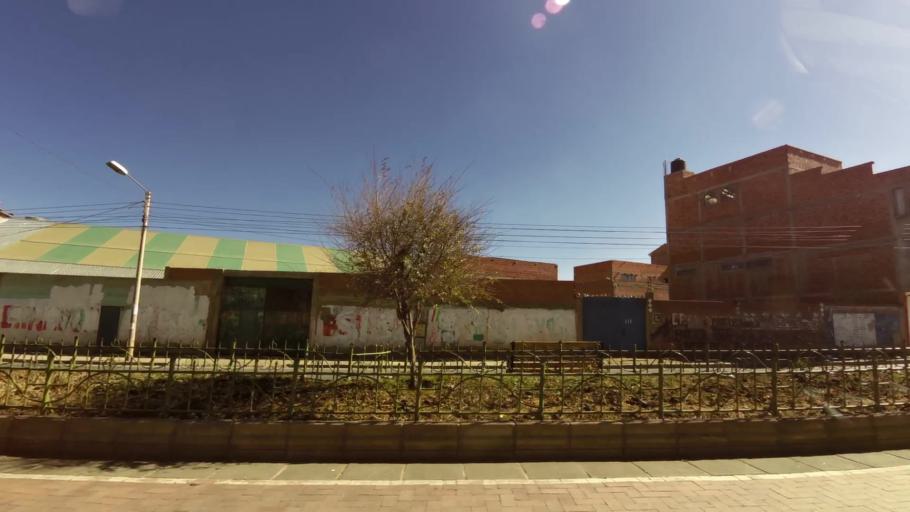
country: BO
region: La Paz
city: La Paz
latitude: -16.5203
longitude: -68.1888
